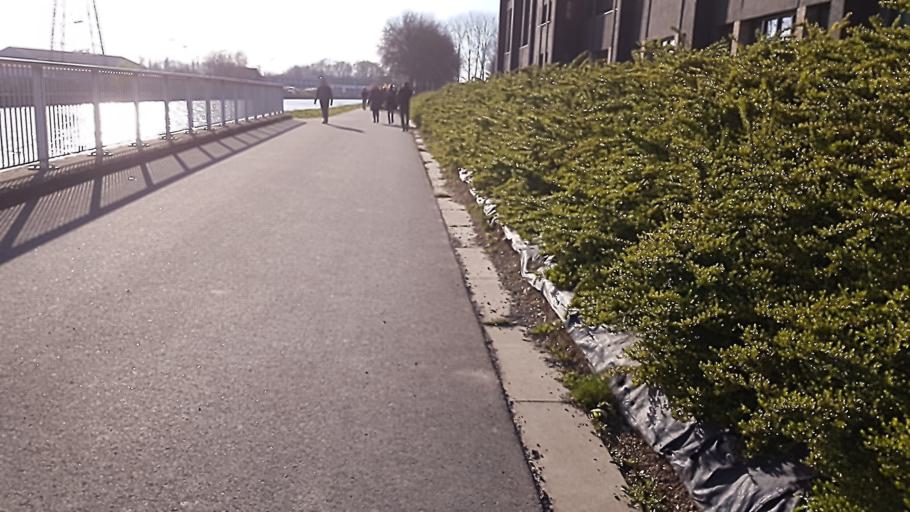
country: BE
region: Flanders
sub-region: Provincie West-Vlaanderen
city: Harelbeke
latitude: 50.8284
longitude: 3.3029
